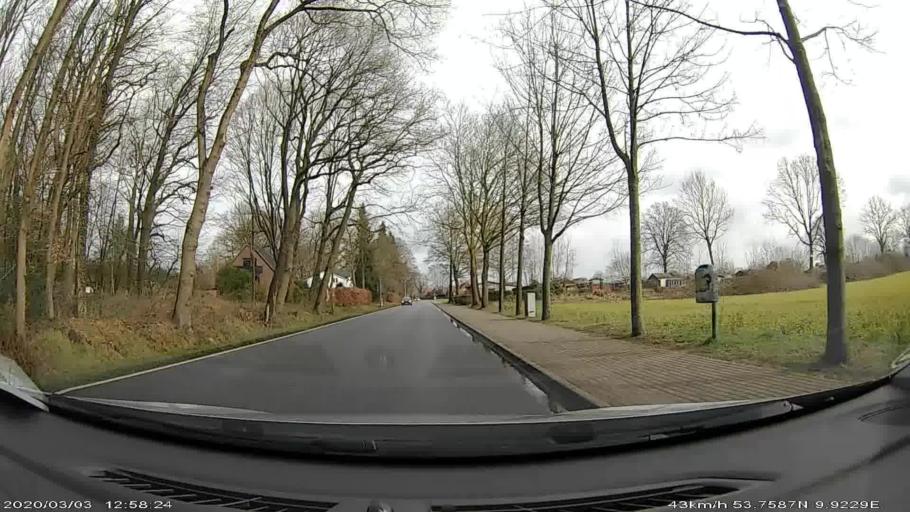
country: DE
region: Schleswig-Holstein
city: Ellerau
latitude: 53.7593
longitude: 9.9244
